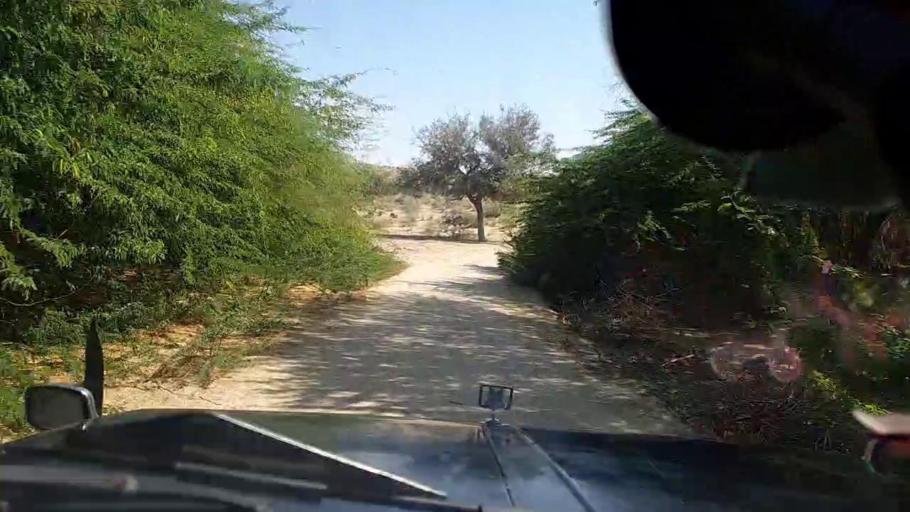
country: PK
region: Sindh
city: Diplo
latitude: 24.3912
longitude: 69.6569
